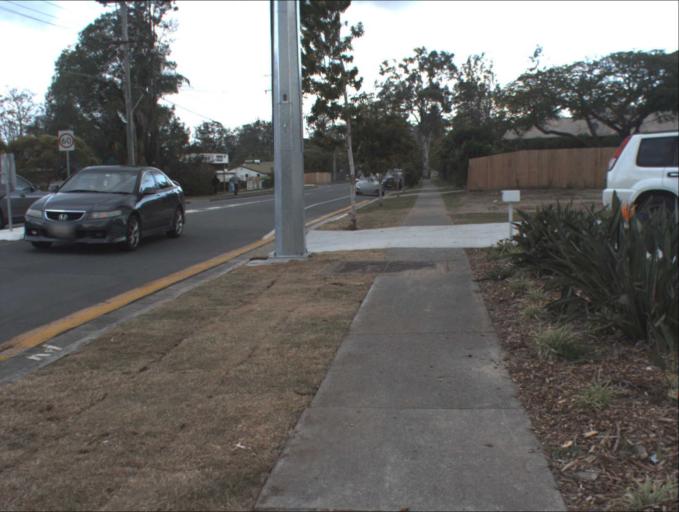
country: AU
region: Queensland
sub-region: Logan
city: Waterford West
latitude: -27.6756
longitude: 153.1310
